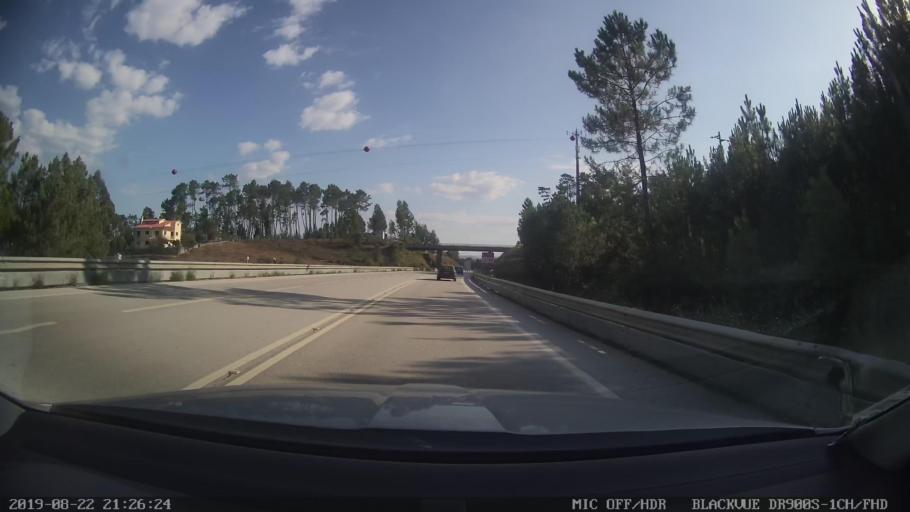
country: PT
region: Leiria
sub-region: Pedrogao Grande
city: Pedrogao Grande
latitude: 39.8667
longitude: -8.1287
